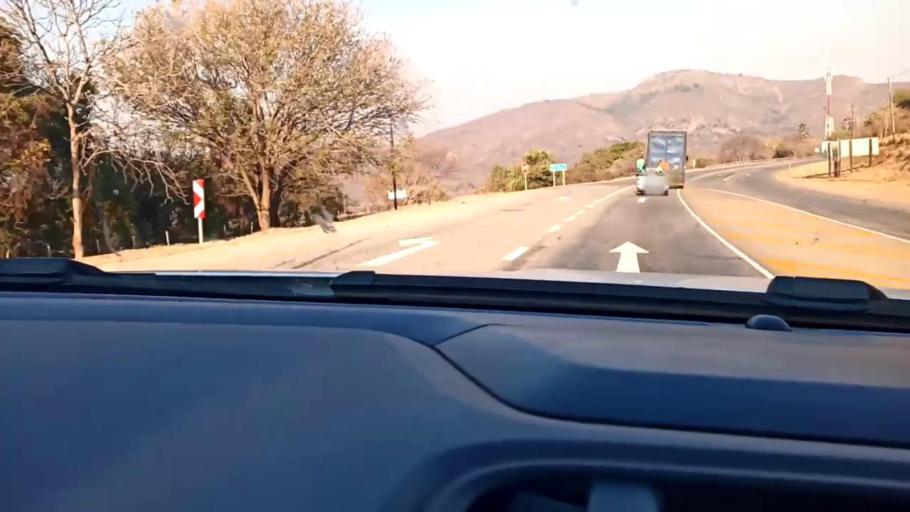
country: ZA
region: Limpopo
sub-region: Mopani District Municipality
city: Duiwelskloof
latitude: -23.6461
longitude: 30.1681
